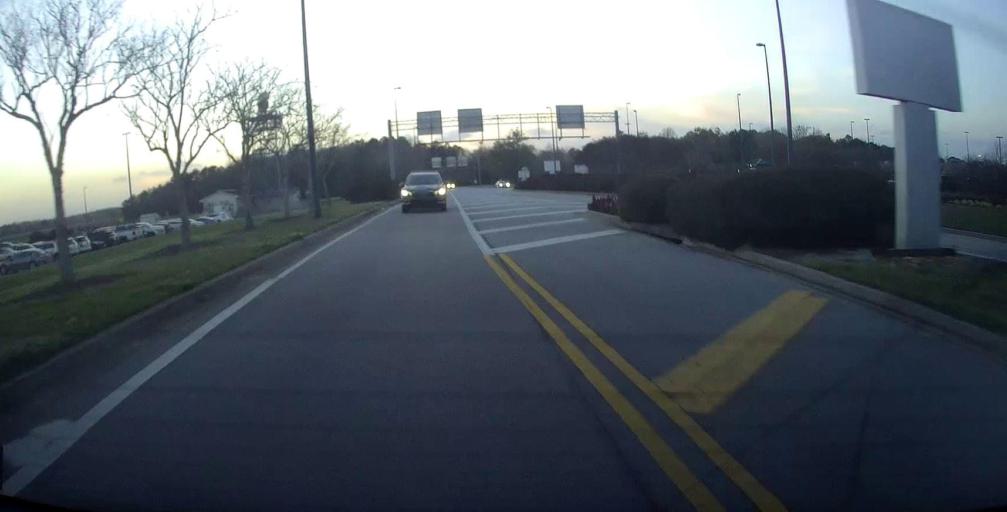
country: US
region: Georgia
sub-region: Chatham County
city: Pooler
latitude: 32.1338
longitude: -81.2118
